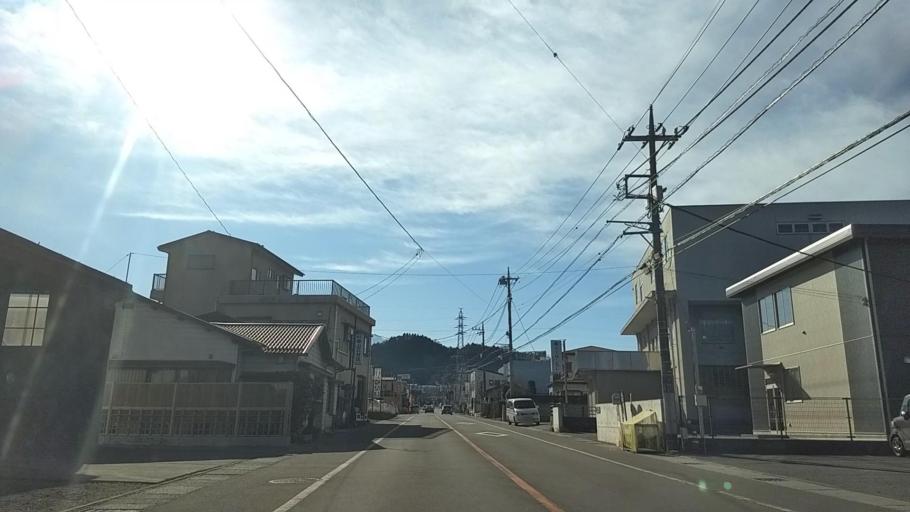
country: JP
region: Yamanashi
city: Otsuki
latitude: 35.5622
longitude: 138.9120
